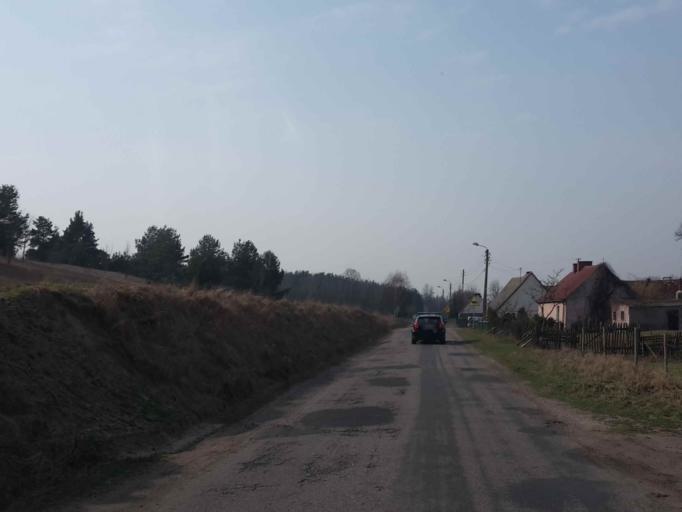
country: PL
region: Kujawsko-Pomorskie
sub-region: Powiat nakielski
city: Sadki
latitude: 53.0957
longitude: 17.4997
